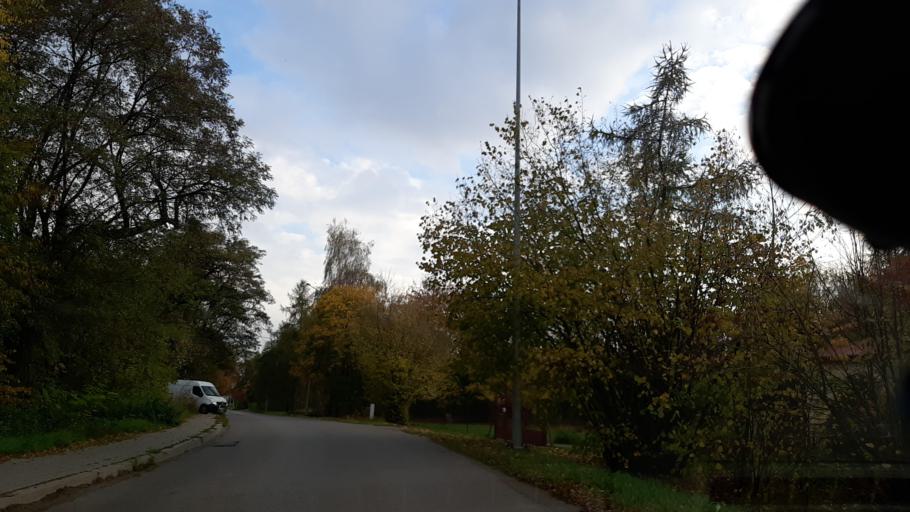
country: PL
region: Lublin Voivodeship
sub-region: Powiat pulawski
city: Naleczow
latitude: 51.3128
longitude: 22.2145
